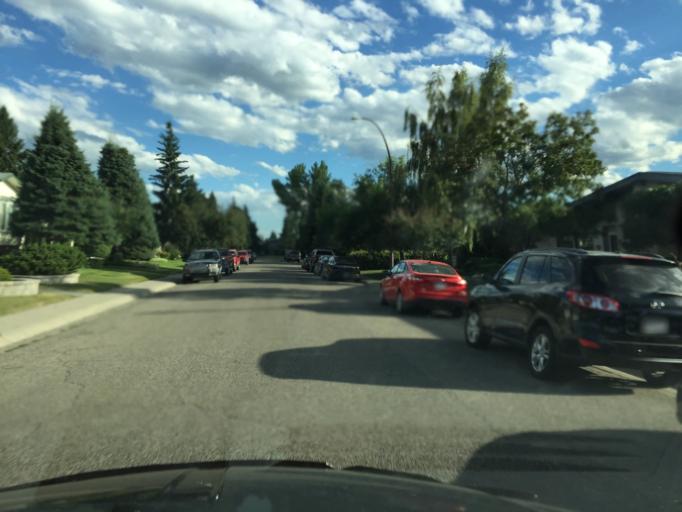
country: CA
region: Alberta
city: Calgary
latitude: 50.9349
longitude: -114.0454
